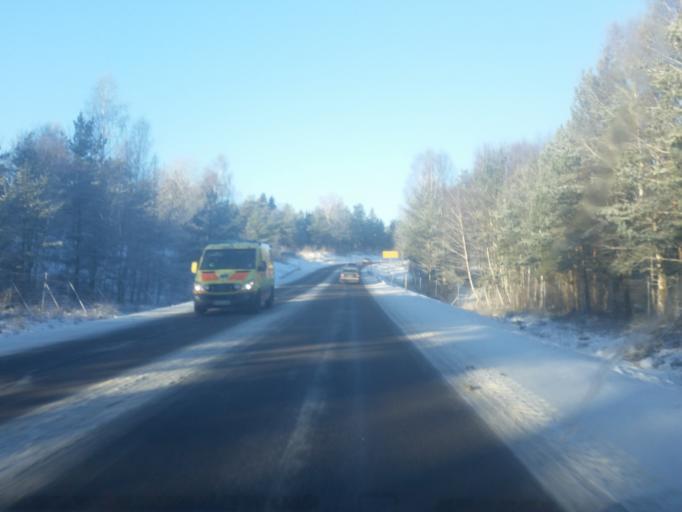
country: SE
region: Vaestra Goetaland
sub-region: Partille Kommun
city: Furulund
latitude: 57.7127
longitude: 12.1462
